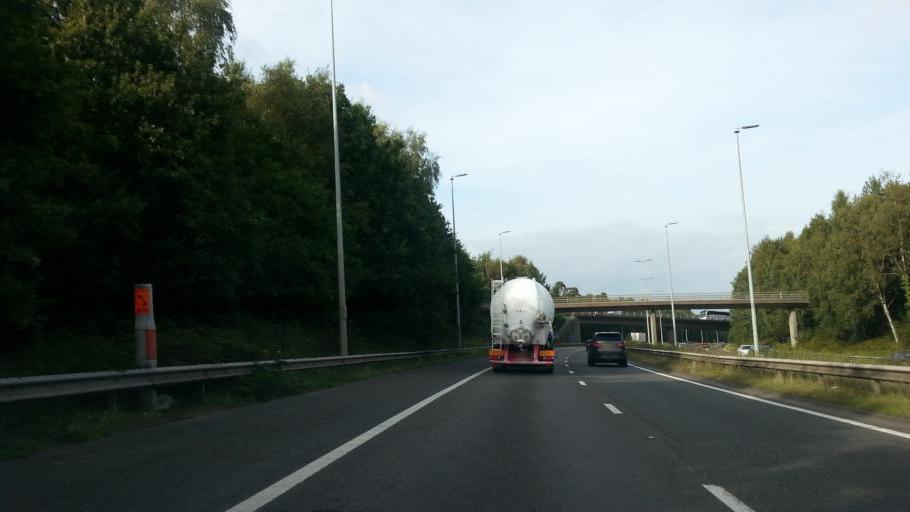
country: GB
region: England
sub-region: Hampshire
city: Eastleigh
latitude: 50.9559
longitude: -1.3996
